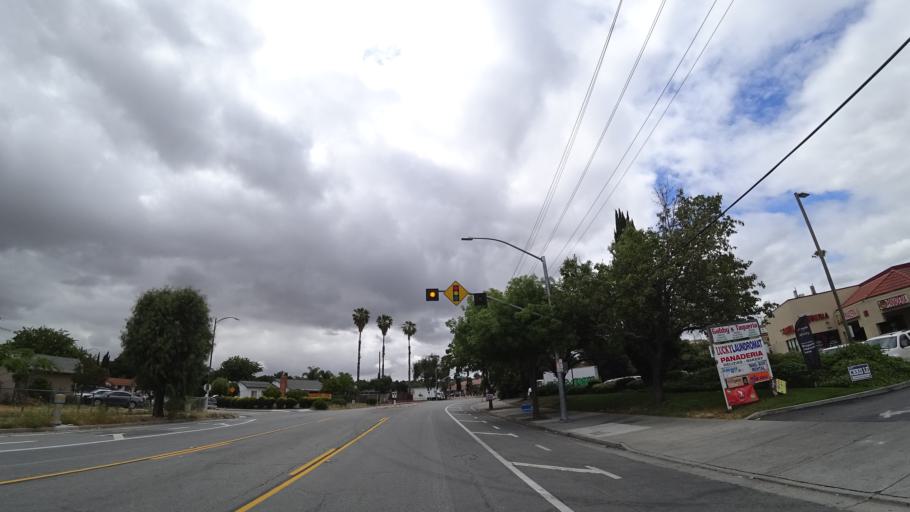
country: US
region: California
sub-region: Santa Clara County
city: Seven Trees
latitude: 37.2834
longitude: -121.8241
